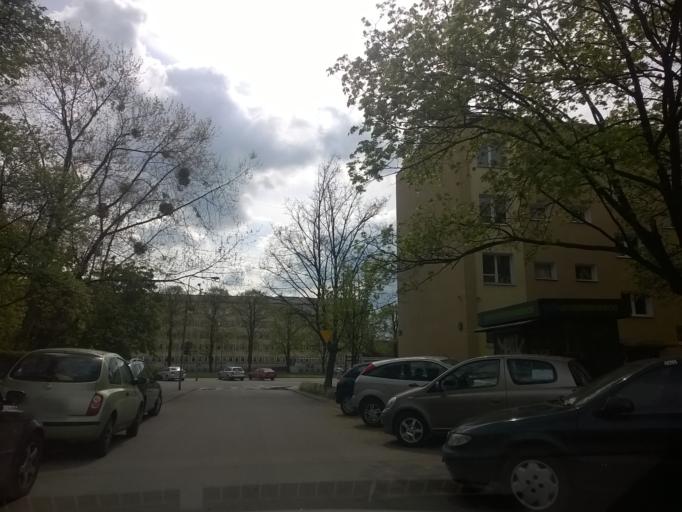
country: PL
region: Masovian Voivodeship
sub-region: Warszawa
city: Mokotow
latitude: 52.1895
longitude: 21.0125
